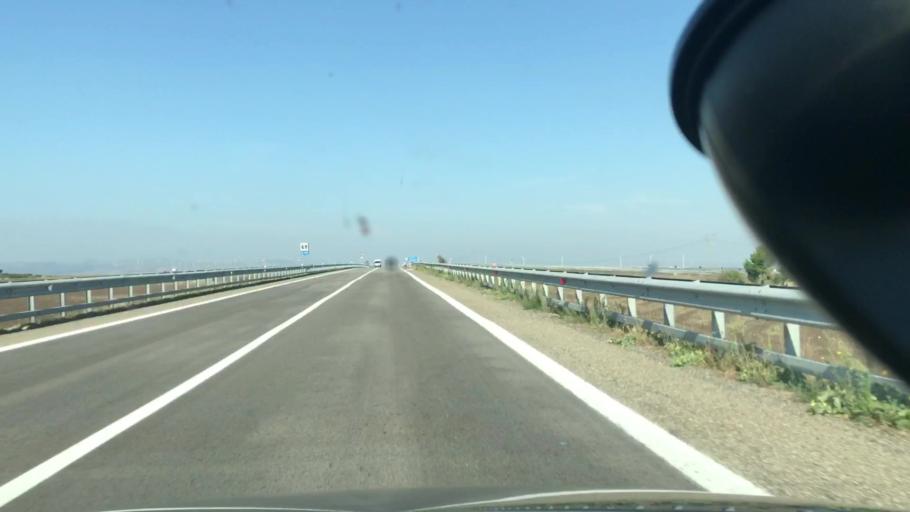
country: IT
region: Basilicate
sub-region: Provincia di Potenza
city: Montemilone
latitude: 40.9929
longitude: 15.8912
